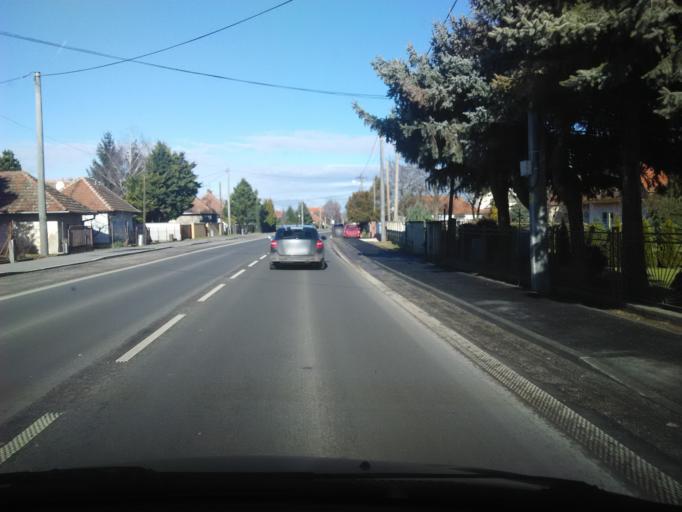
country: SK
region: Nitriansky
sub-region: Okres Nitra
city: Nitra
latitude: 48.2453
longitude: 18.1124
